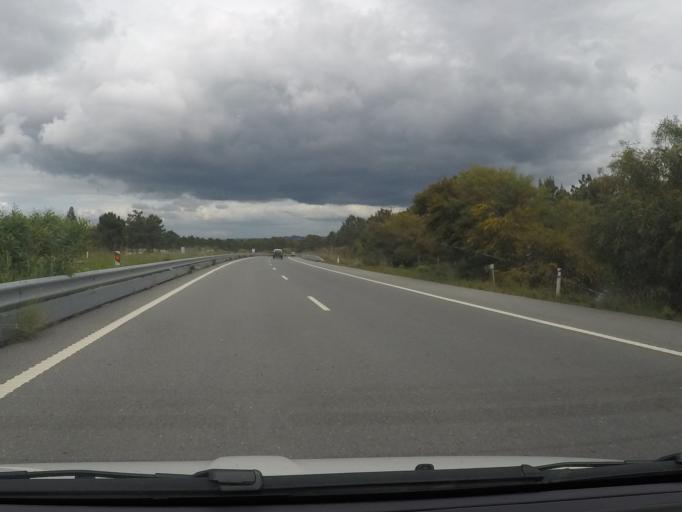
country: PT
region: Setubal
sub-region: Sines
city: Sines
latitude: 37.9776
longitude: -8.8009
